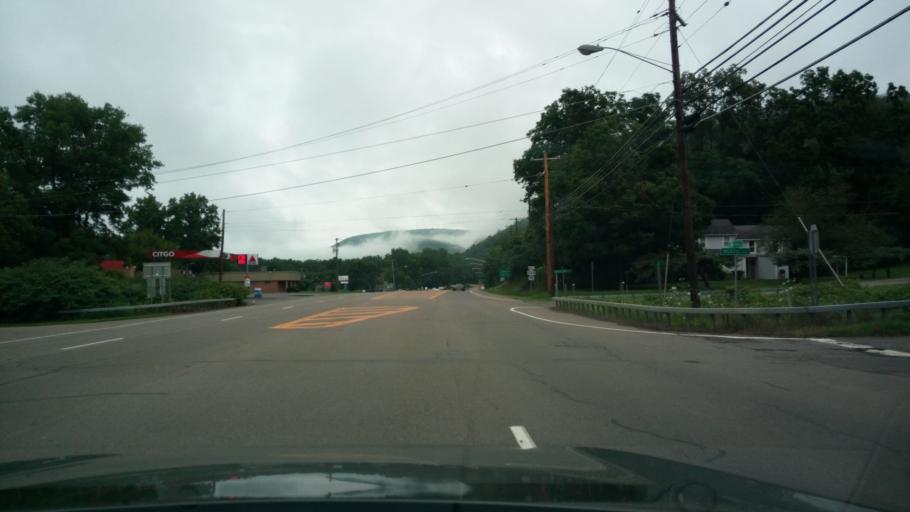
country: US
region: New York
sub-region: Chemung County
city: West Elmira
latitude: 42.0831
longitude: -76.8610
